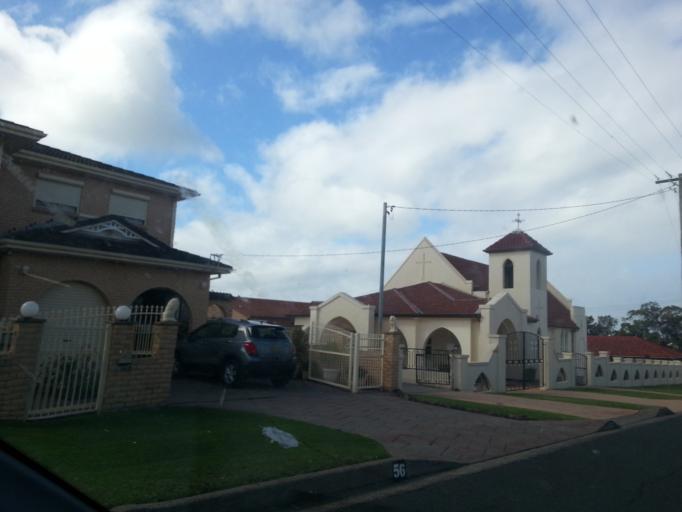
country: AU
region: New South Wales
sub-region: Wollongong
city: Port Kembla
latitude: -34.4847
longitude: 150.9006
